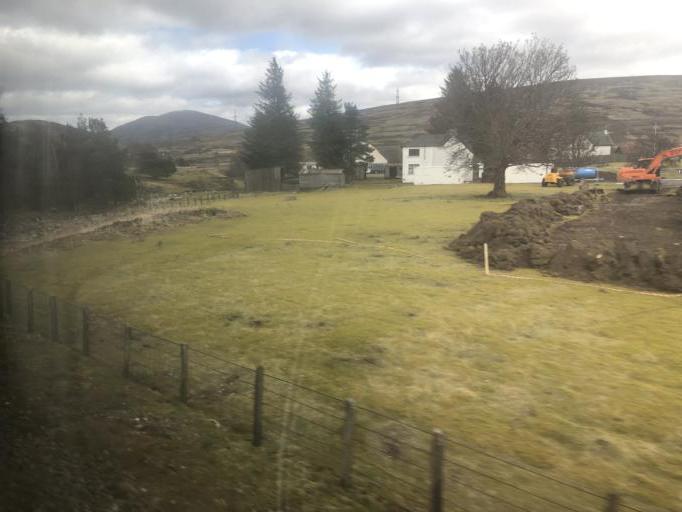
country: GB
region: Scotland
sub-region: Highland
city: Kingussie
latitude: 56.9410
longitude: -4.2400
